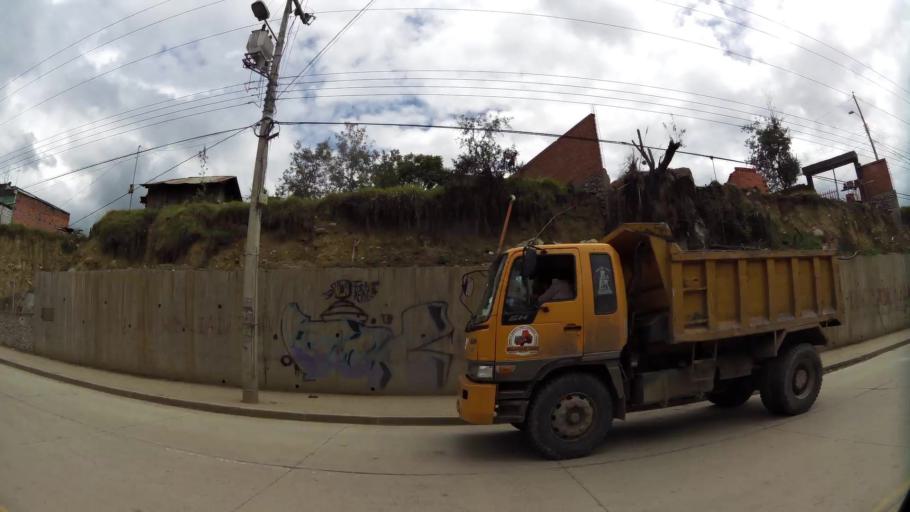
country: EC
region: Azuay
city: Cuenca
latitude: -2.8794
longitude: -79.0679
